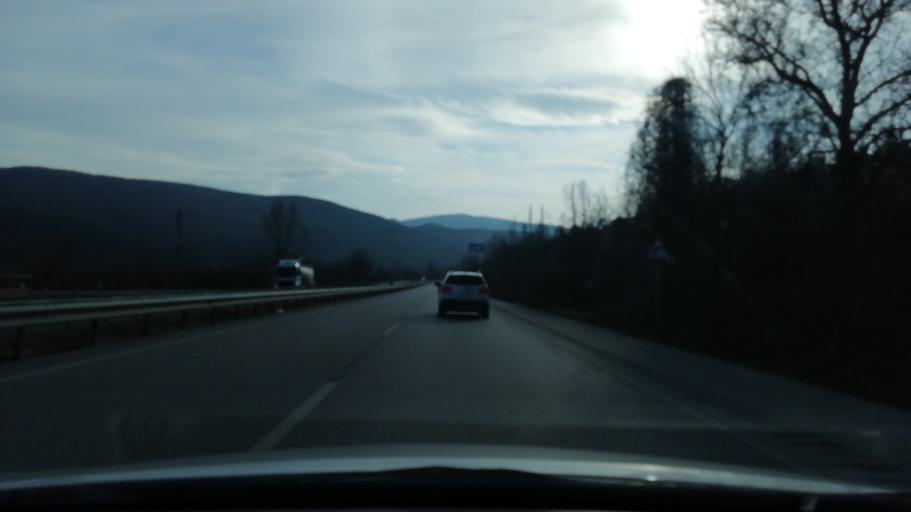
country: TR
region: Karabuk
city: Eskipazar
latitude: 41.0156
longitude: 32.6259
